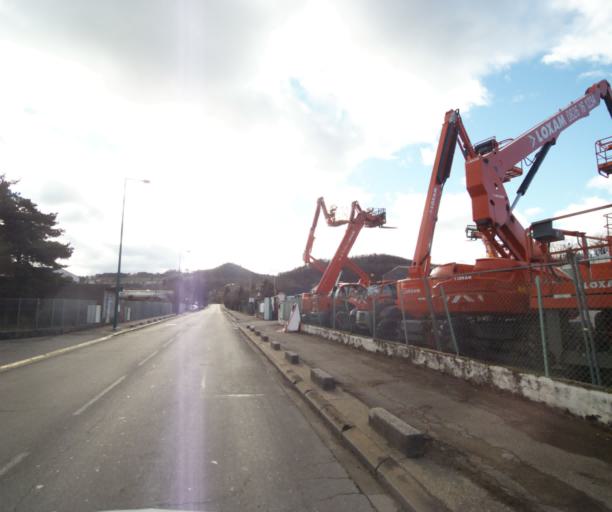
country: FR
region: Rhone-Alpes
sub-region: Departement de la Loire
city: La Talaudiere
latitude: 45.4725
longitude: 4.4322
